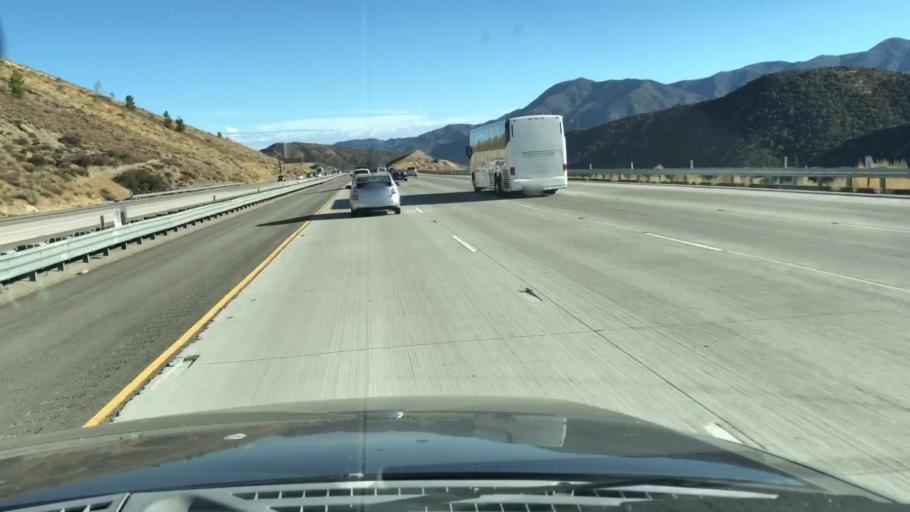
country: US
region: California
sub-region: Kern County
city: Lebec
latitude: 34.6940
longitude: -118.7906
